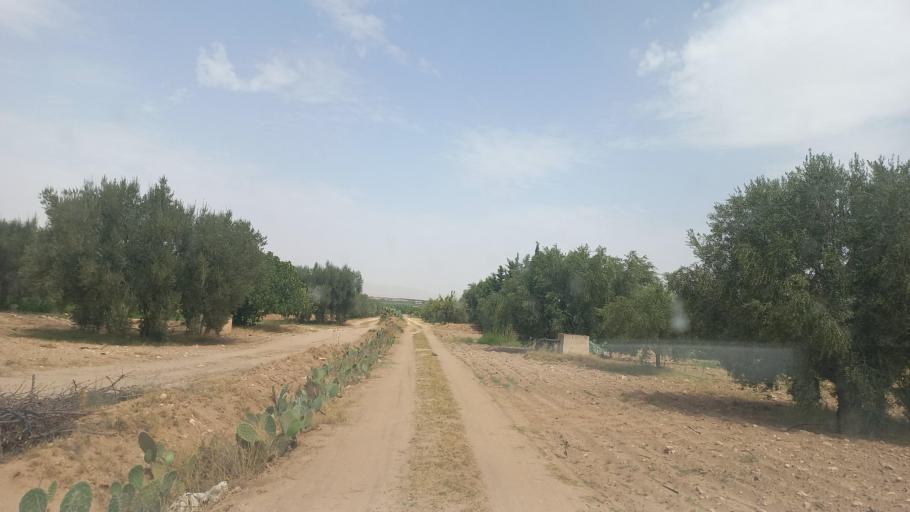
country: TN
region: Al Qasrayn
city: Kasserine
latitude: 35.2622
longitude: 9.0002
